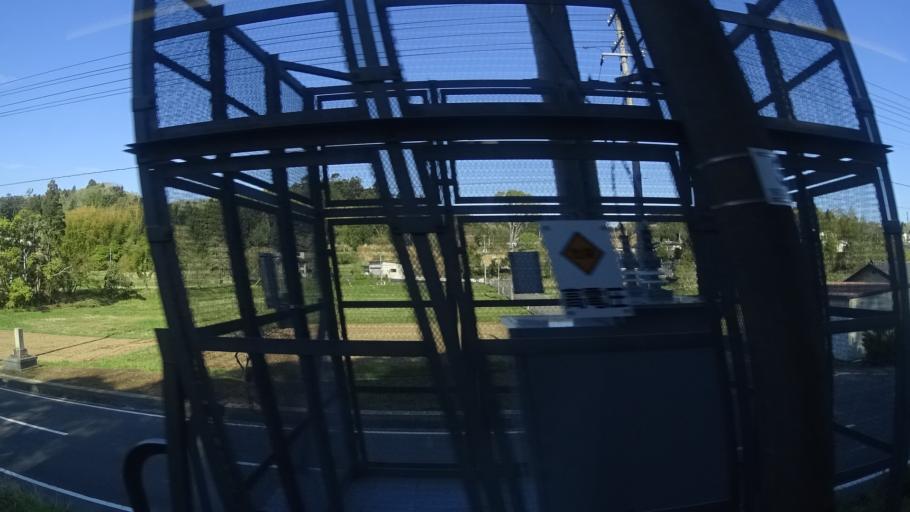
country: JP
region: Fukushima
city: Namie
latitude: 37.5527
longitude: 140.9946
